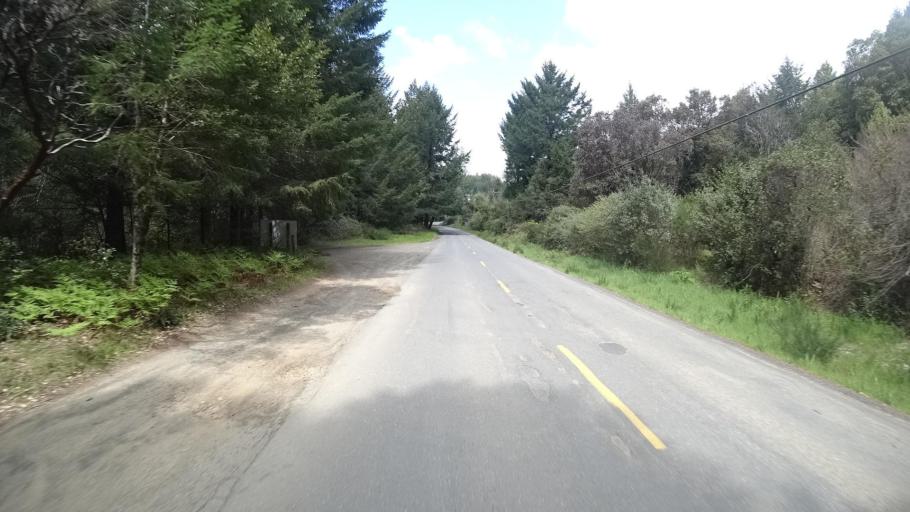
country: US
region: California
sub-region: Humboldt County
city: Redway
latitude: 40.0608
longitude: -123.9602
